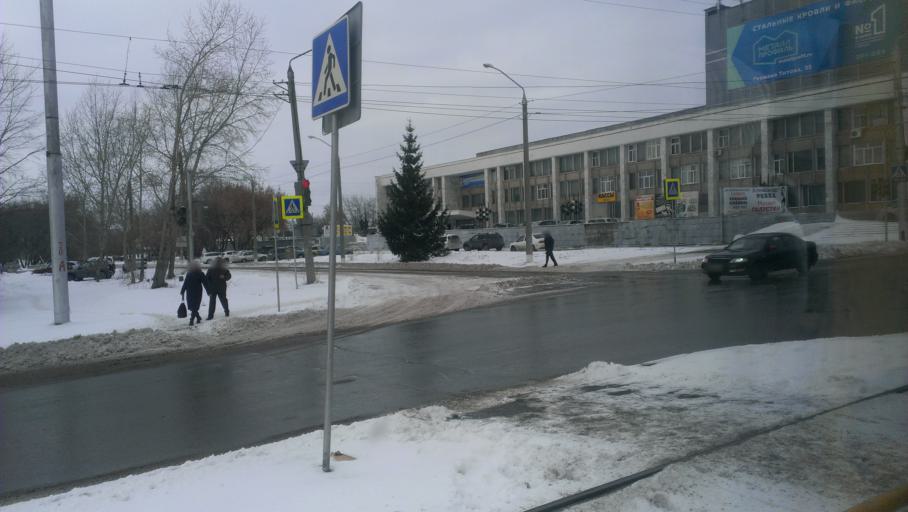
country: RU
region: Altai Krai
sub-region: Gorod Barnaulskiy
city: Barnaul
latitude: 53.3824
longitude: 83.7131
